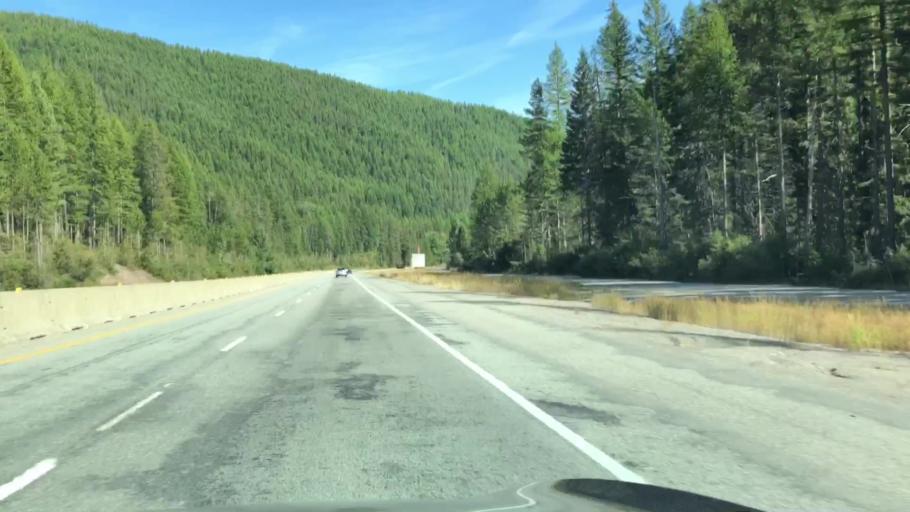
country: US
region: Idaho
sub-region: Shoshone County
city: Wallace
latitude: 47.4316
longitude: -115.6486
